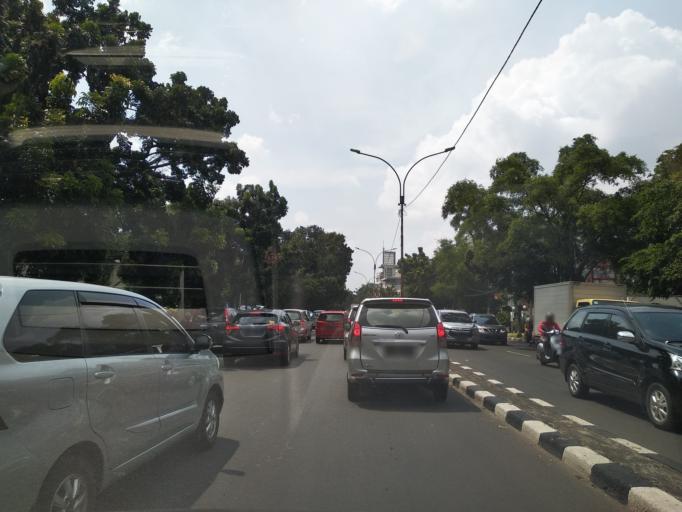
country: ID
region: Jakarta Raya
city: Jakarta
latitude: -6.2284
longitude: 106.8474
